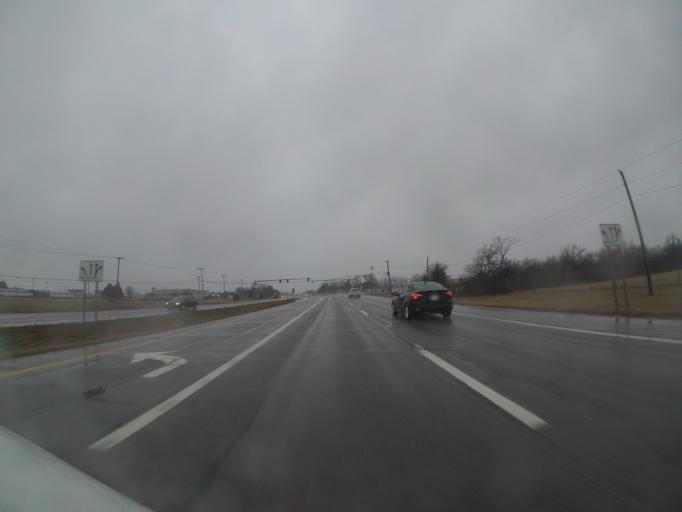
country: US
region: Ohio
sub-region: Wood County
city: Rossford
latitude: 41.5648
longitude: -83.5560
